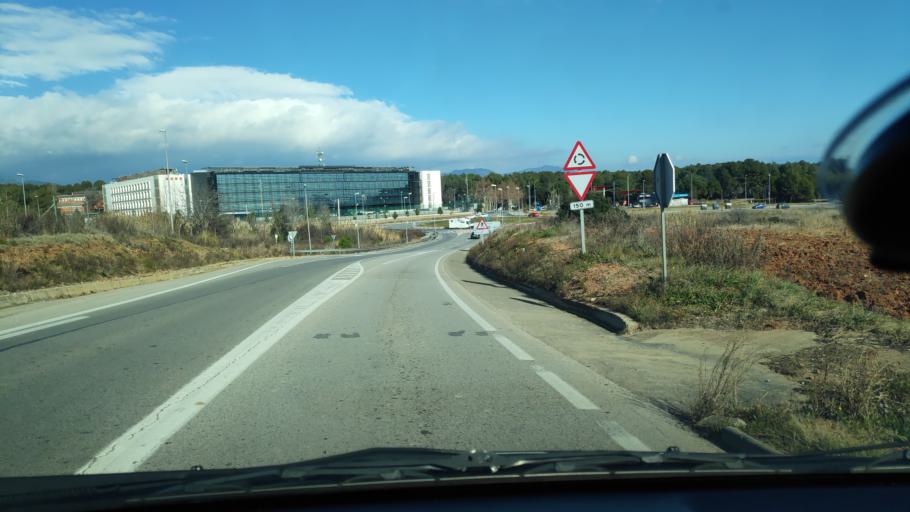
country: ES
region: Catalonia
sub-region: Provincia de Barcelona
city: Sant Quirze del Valles
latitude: 41.5512
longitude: 2.0674
